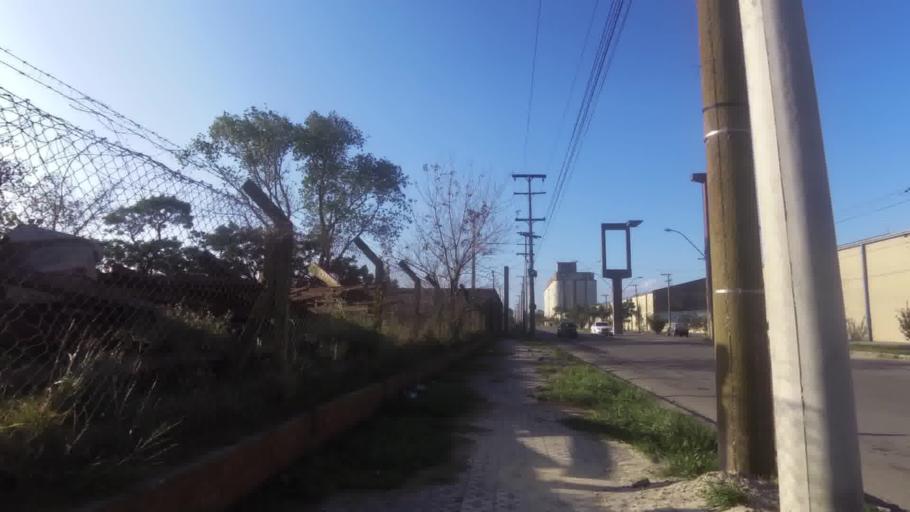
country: BR
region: Rio Grande do Sul
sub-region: Rio Grande
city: Rio Grande
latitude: -32.0392
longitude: -52.0778
